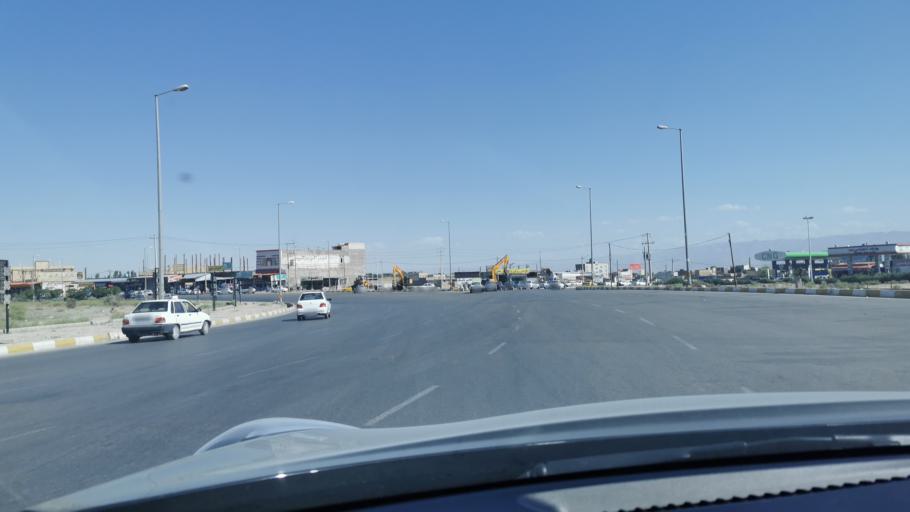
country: IR
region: Razavi Khorasan
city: Chenaran
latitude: 36.6336
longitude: 59.1326
